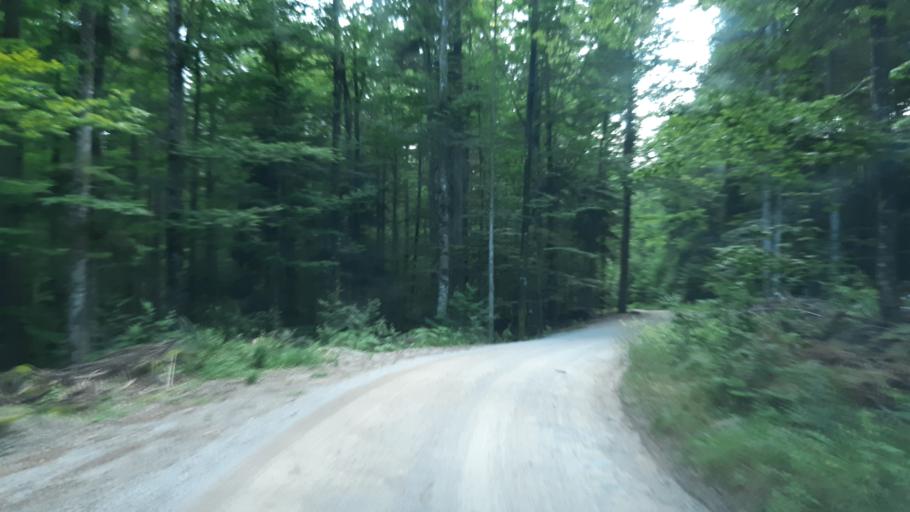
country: SI
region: Kocevje
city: Kocevje
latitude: 45.6688
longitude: 14.9711
